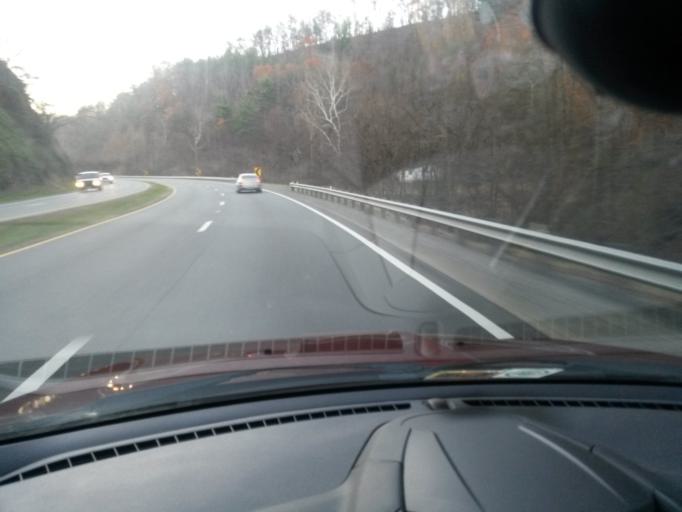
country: US
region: Virginia
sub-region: Roanoke County
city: Narrows
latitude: 37.1956
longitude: -79.9425
